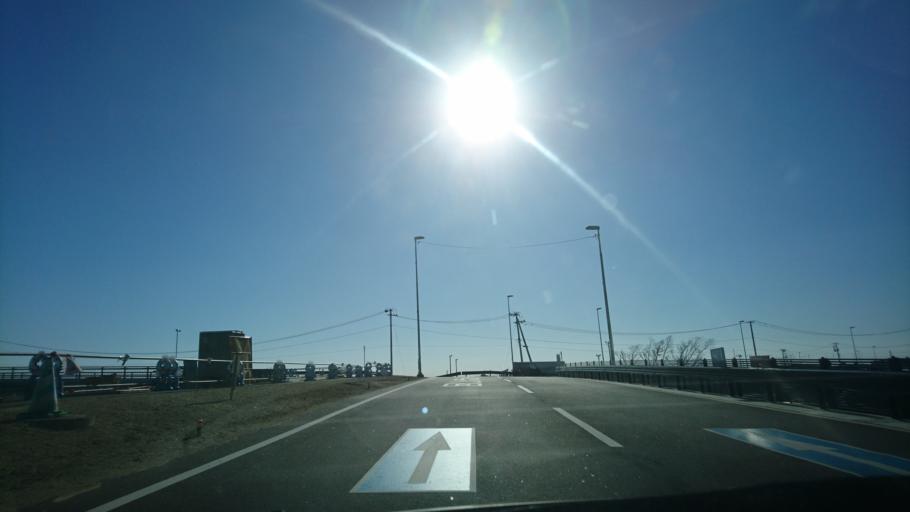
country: JP
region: Miyagi
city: Iwanuma
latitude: 38.1374
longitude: 140.9320
